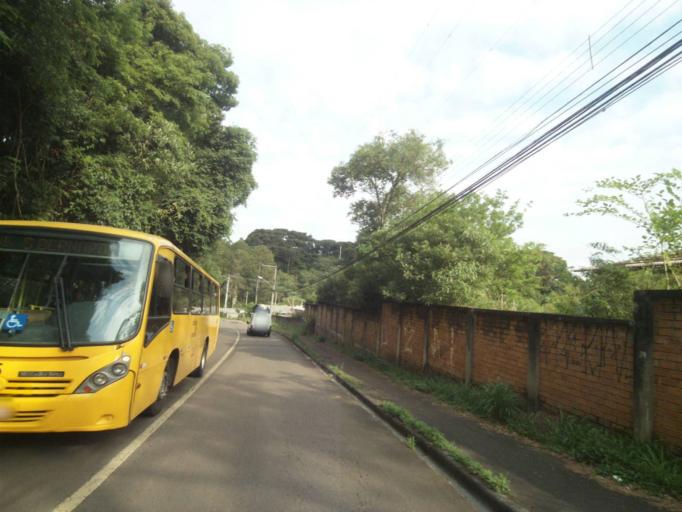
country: BR
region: Parana
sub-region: Curitiba
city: Curitiba
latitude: -25.4104
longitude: -49.3083
